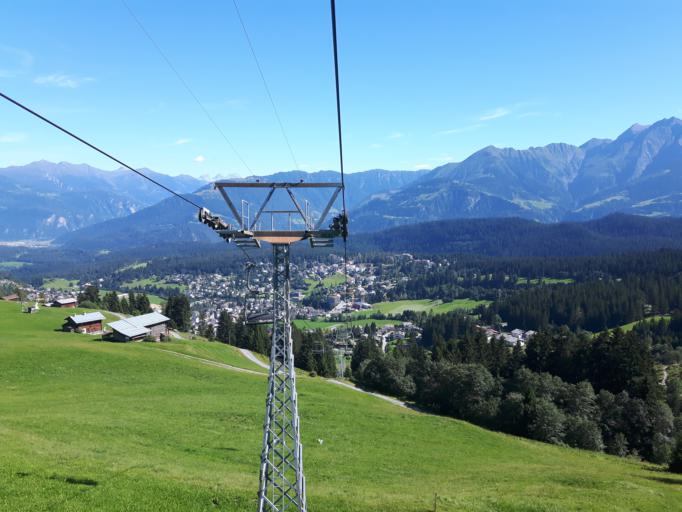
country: CH
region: Grisons
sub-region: Imboden District
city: Flims
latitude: 46.8442
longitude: 9.2702
